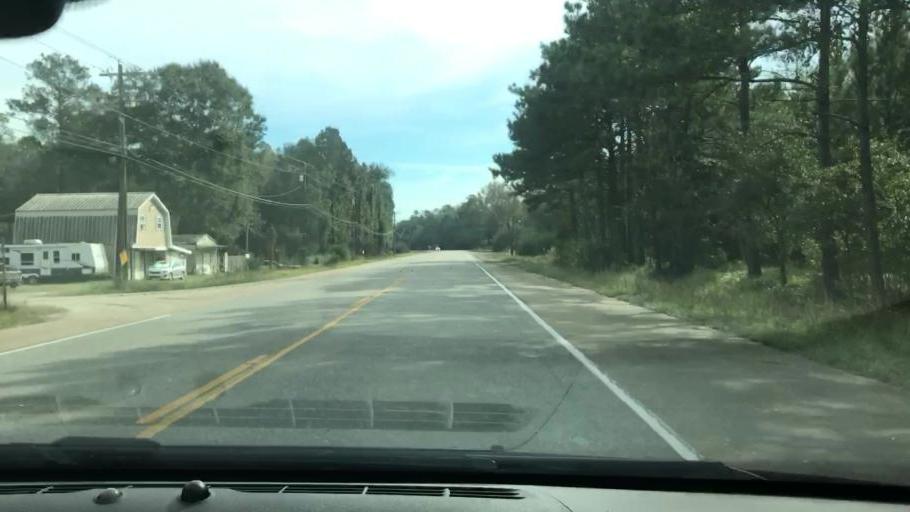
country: US
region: Louisiana
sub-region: Saint Tammany Parish
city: Pearl River
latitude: 30.4090
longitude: -89.7754
